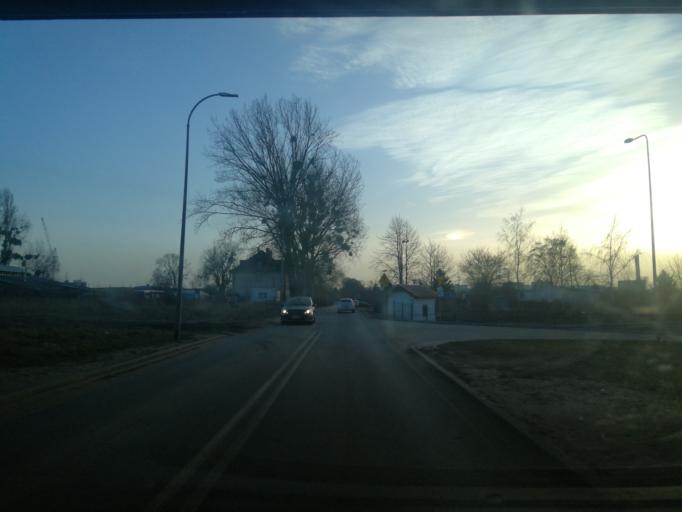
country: PL
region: Pomeranian Voivodeship
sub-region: Gdansk
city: Gdansk
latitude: 54.3945
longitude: 18.6371
